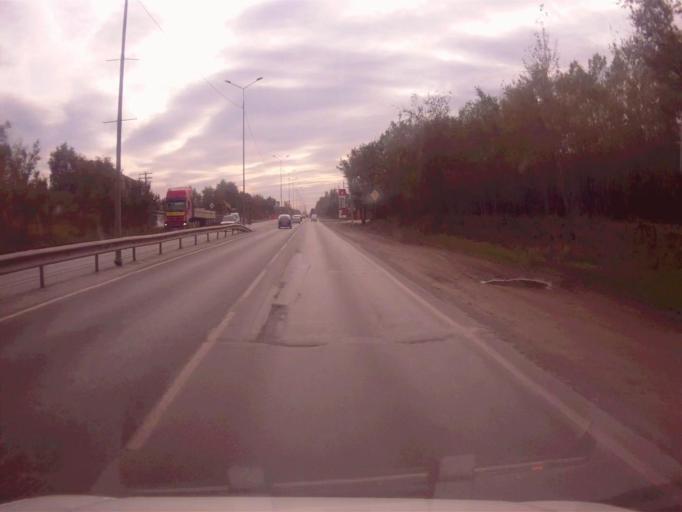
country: RU
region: Chelyabinsk
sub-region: Gorod Chelyabinsk
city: Chelyabinsk
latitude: 55.1080
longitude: 61.4083
